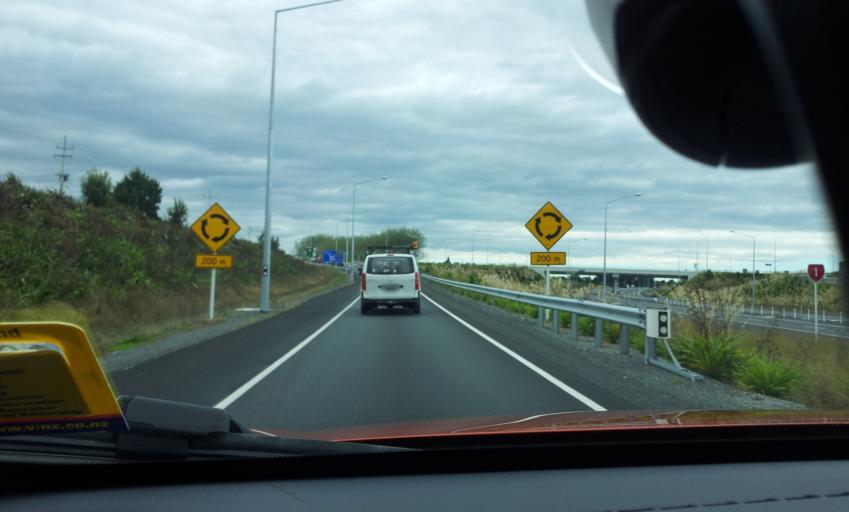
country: NZ
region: Waikato
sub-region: Waikato District
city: Ngaruawahia
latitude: -37.7103
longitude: 175.2069
